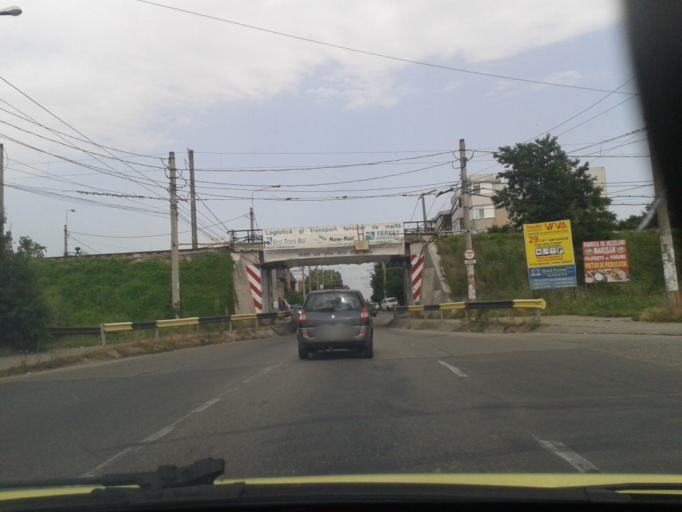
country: RO
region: Prahova
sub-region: Comuna Targsoru Vechi
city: Strejnicu
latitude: 44.9391
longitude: 25.9801
